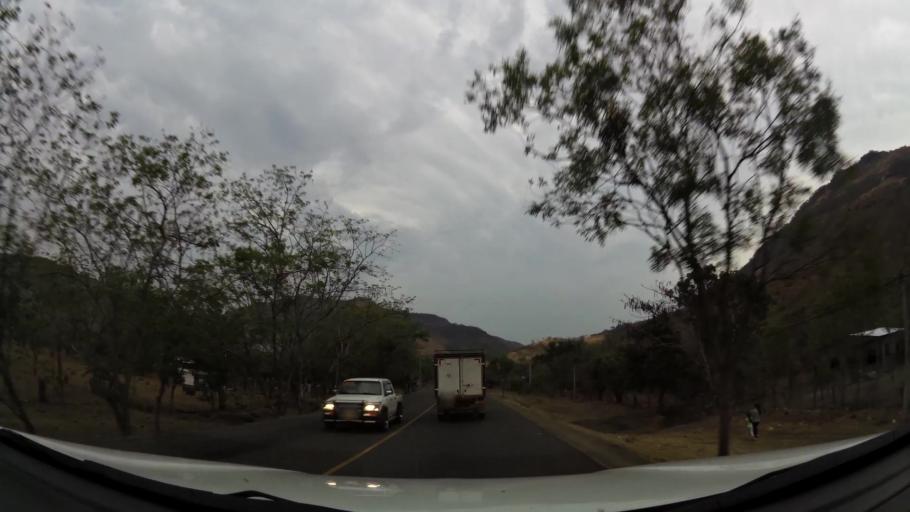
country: NI
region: Leon
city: Santa Rosa del Penon
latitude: 12.9364
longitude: -86.2035
